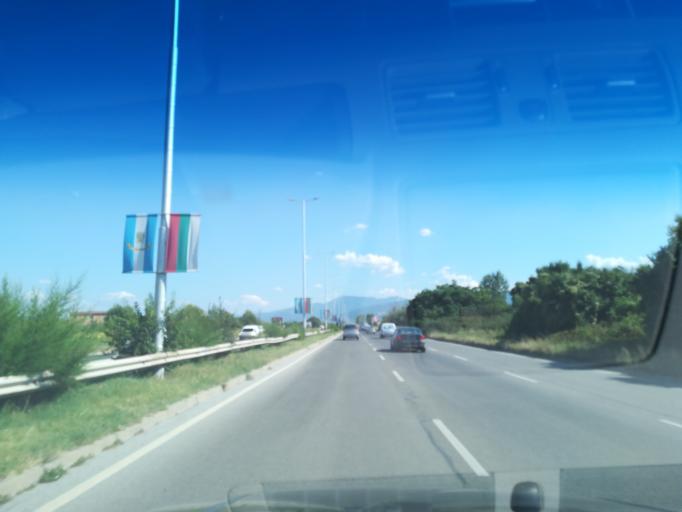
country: BG
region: Plovdiv
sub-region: Obshtina Plovdiv
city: Plovdiv
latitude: 42.1063
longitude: 24.7832
